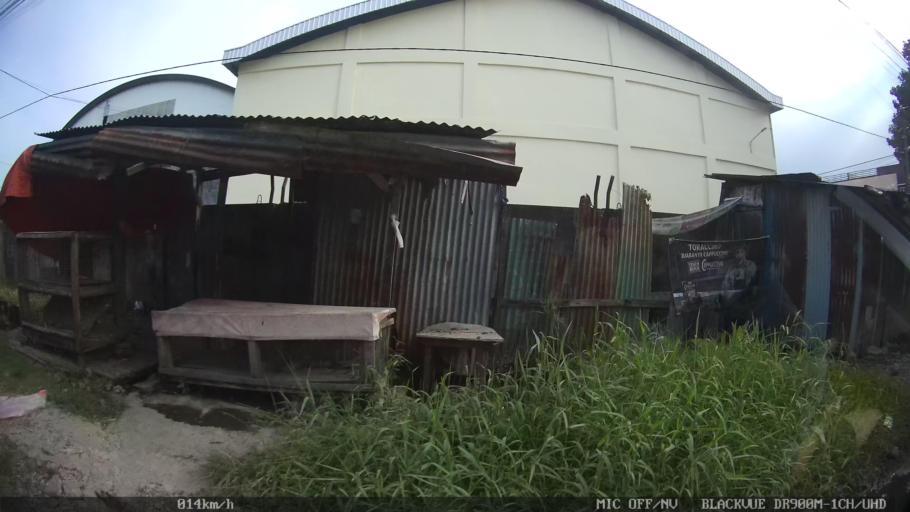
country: ID
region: North Sumatra
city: Medan
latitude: 3.6054
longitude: 98.7384
